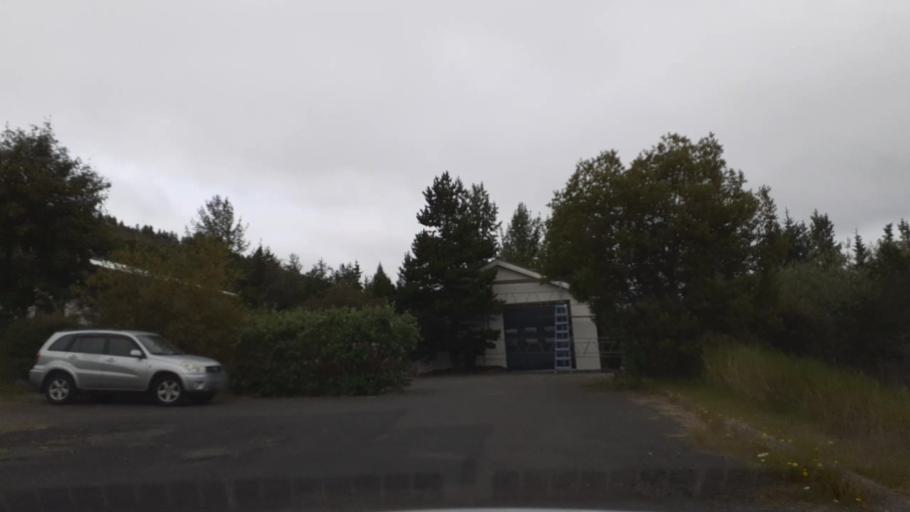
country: IS
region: Northwest
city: Saudarkrokur
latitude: 65.5552
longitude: -19.4507
